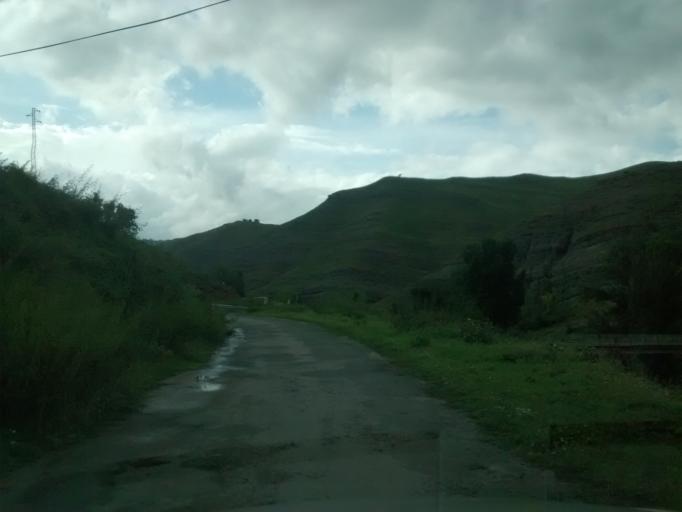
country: ES
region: La Rioja
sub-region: Provincia de La Rioja
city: San Roman de Cameros
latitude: 42.2178
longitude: -2.4663
